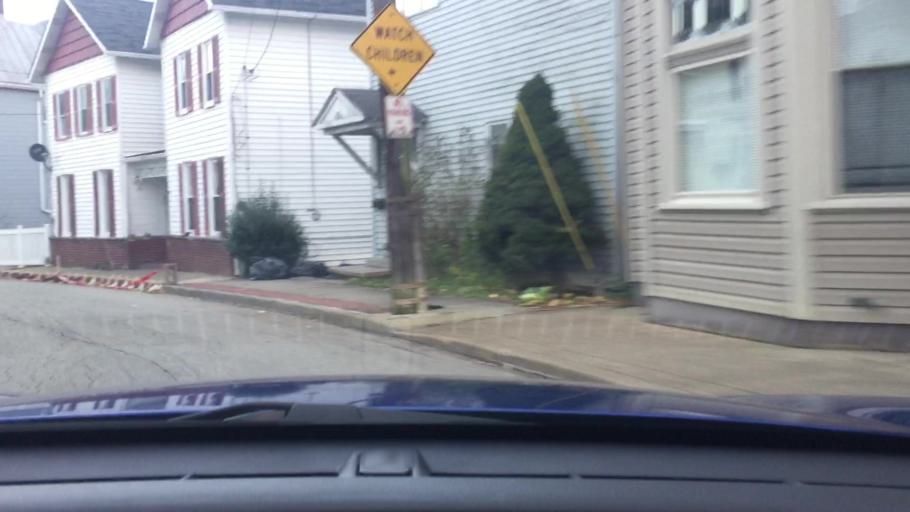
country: US
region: Pennsylvania
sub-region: Westmoreland County
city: Greensburg
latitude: 40.2986
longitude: -79.5422
